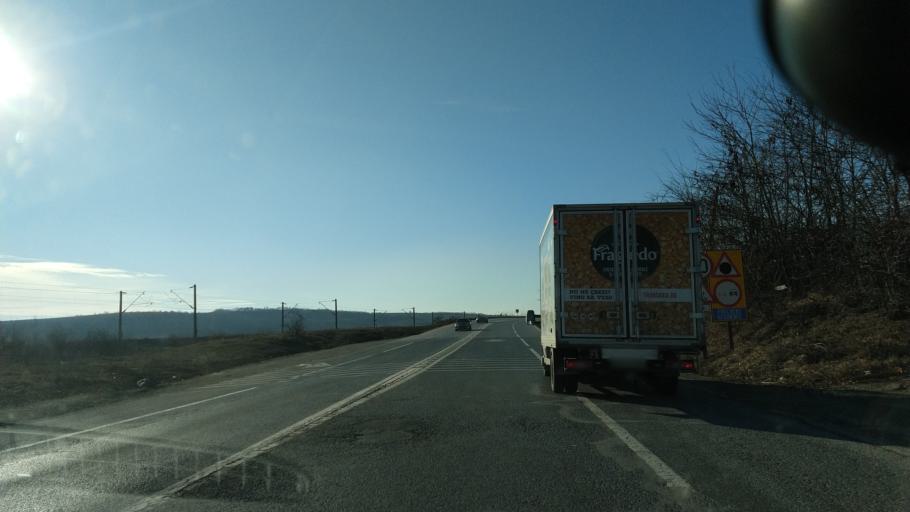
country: RO
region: Iasi
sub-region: Comuna Baltati
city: Baltati
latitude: 47.2231
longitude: 27.1773
